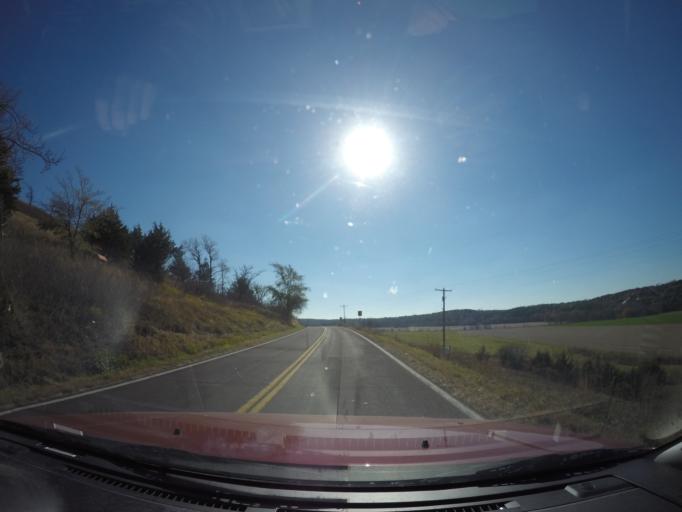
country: US
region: Kansas
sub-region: Geary County
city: Grandview Plaza
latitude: 38.9948
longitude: -96.7304
